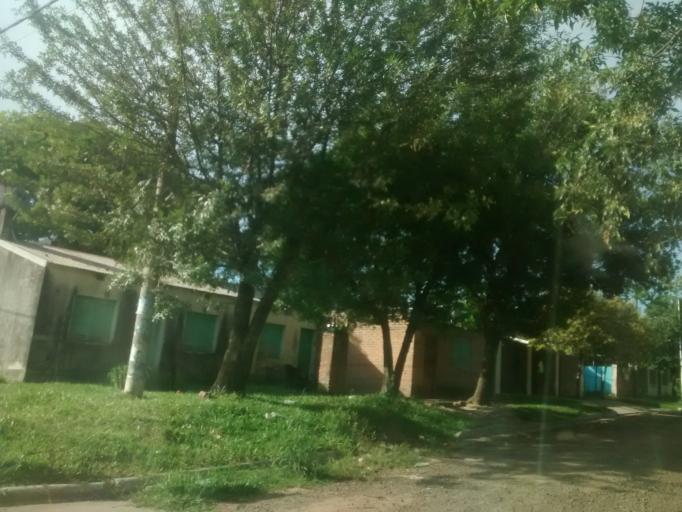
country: AR
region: Chaco
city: Puerto Tirol
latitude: -27.3747
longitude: -59.0917
